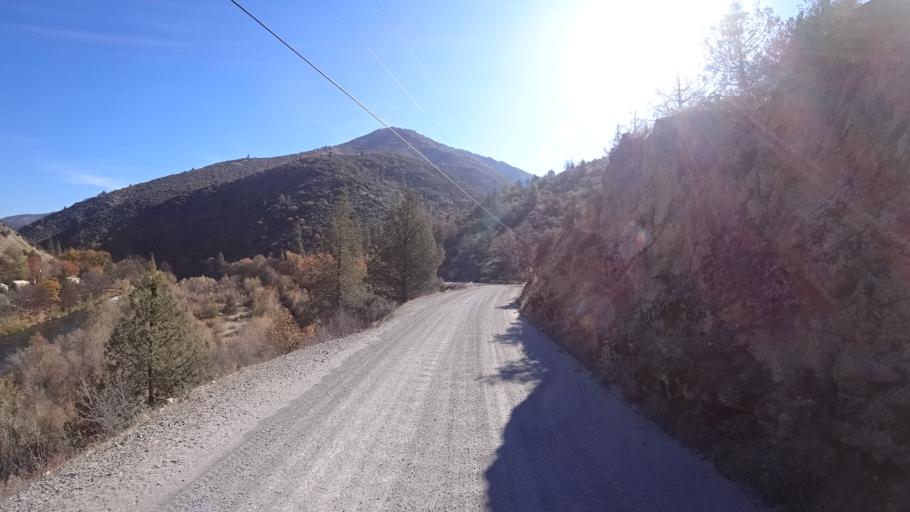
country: US
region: California
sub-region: Siskiyou County
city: Yreka
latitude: 41.8322
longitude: -122.6336
